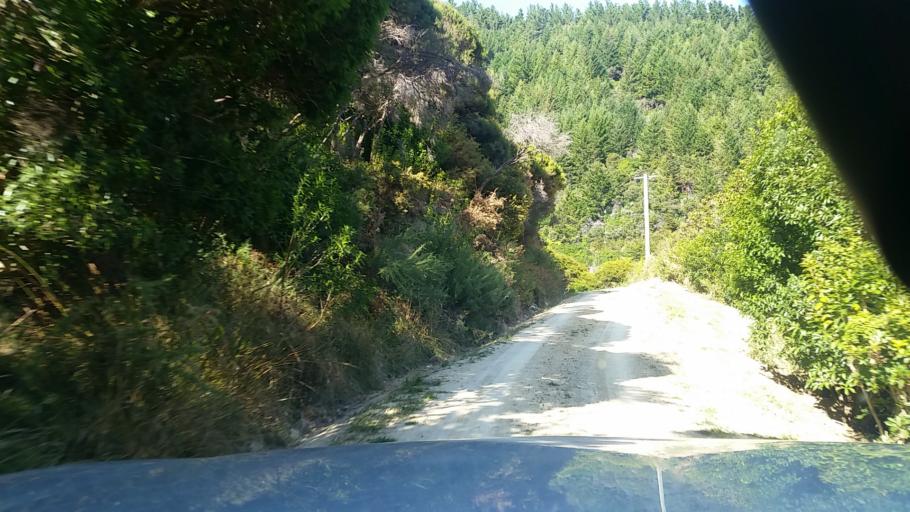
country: NZ
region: Marlborough
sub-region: Marlborough District
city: Picton
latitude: -41.3140
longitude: 174.1750
